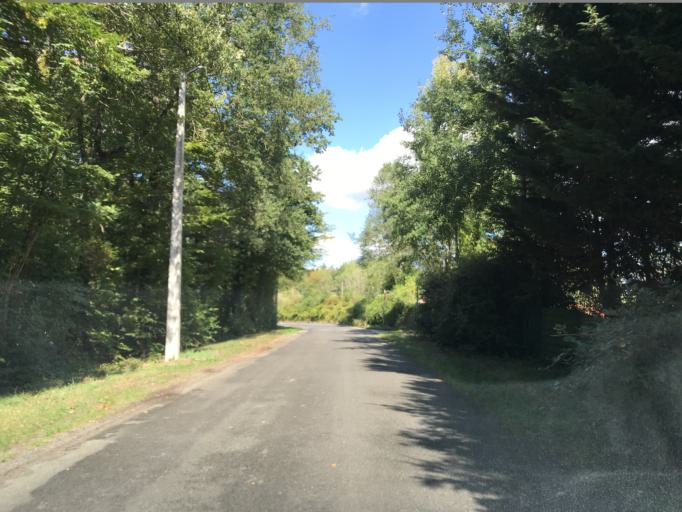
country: FR
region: Haute-Normandie
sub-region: Departement de l'Eure
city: La Chapelle-Reanville
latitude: 49.0892
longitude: 1.3962
